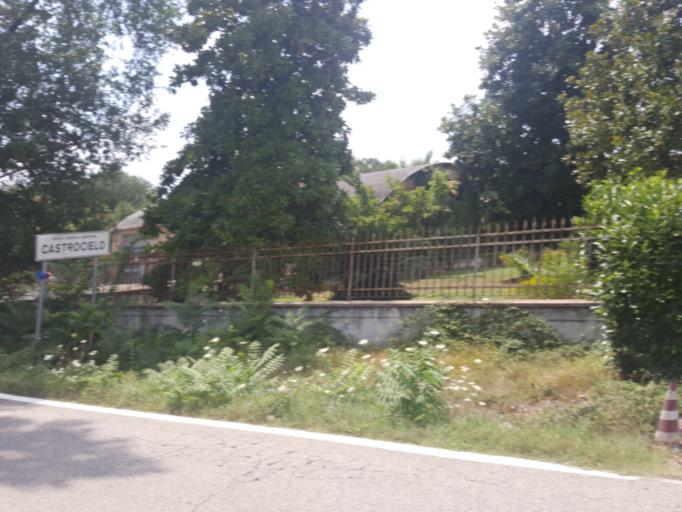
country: IT
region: Latium
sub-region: Provincia di Frosinone
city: Aquino
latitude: 41.5007
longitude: 13.6824
